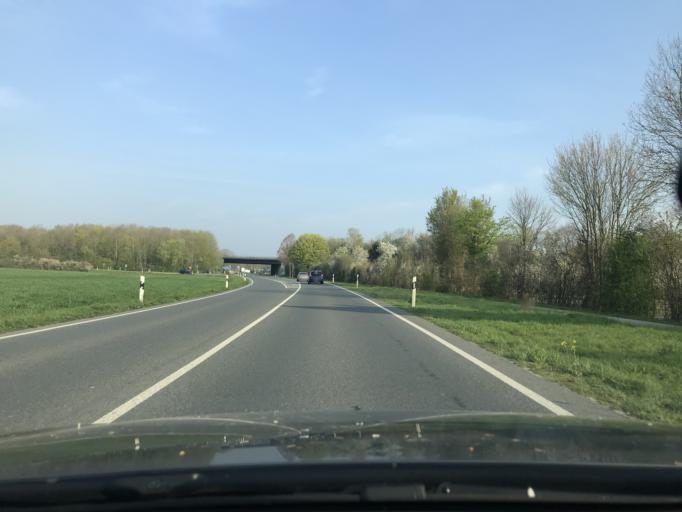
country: DE
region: North Rhine-Westphalia
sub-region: Regierungsbezirk Dusseldorf
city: Weeze
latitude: 51.6537
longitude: 6.1829
